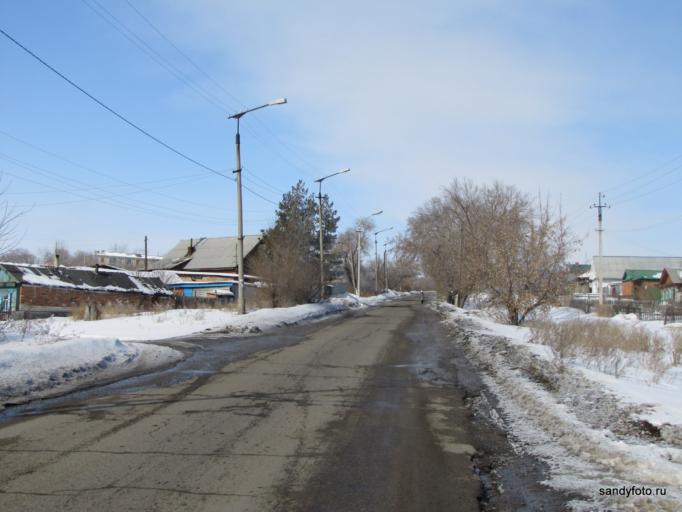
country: RU
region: Chelyabinsk
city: Troitsk
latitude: 54.0978
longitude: 61.5610
